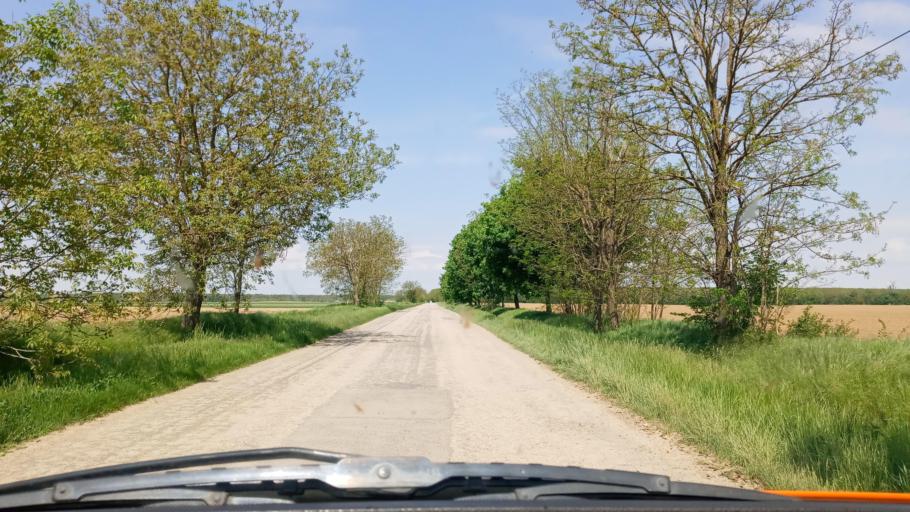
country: HU
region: Baranya
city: Boly
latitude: 45.8764
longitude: 18.5787
